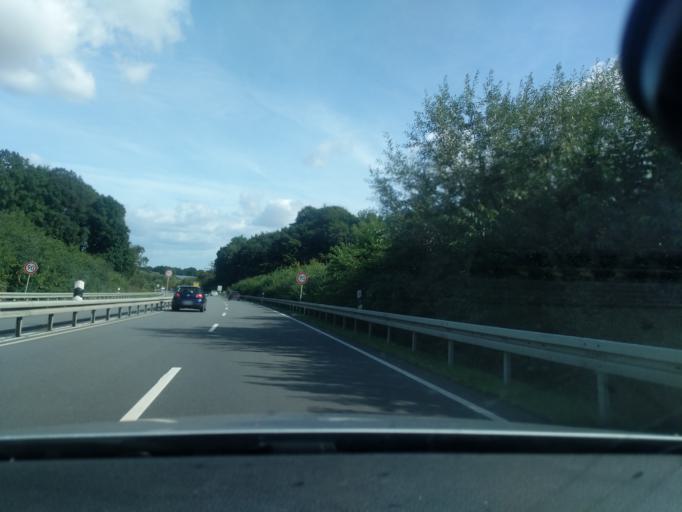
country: DE
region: Lower Saxony
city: Ostercappeln
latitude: 52.3404
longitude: 8.2414
